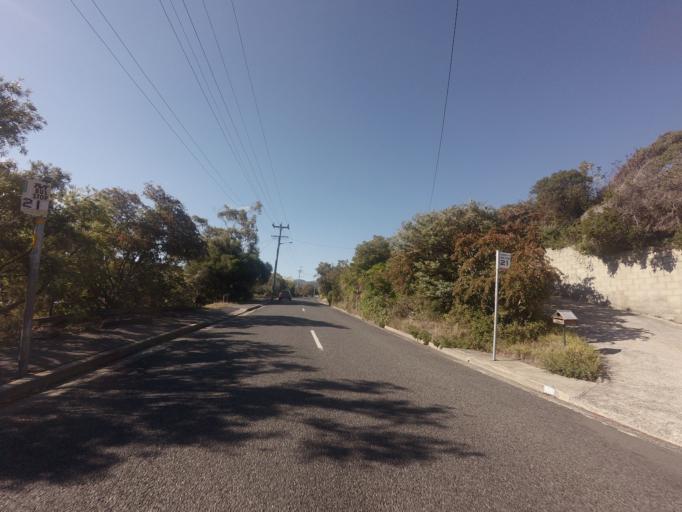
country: AU
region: Tasmania
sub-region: Clarence
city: Lindisfarne
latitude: -42.8424
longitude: 147.3405
